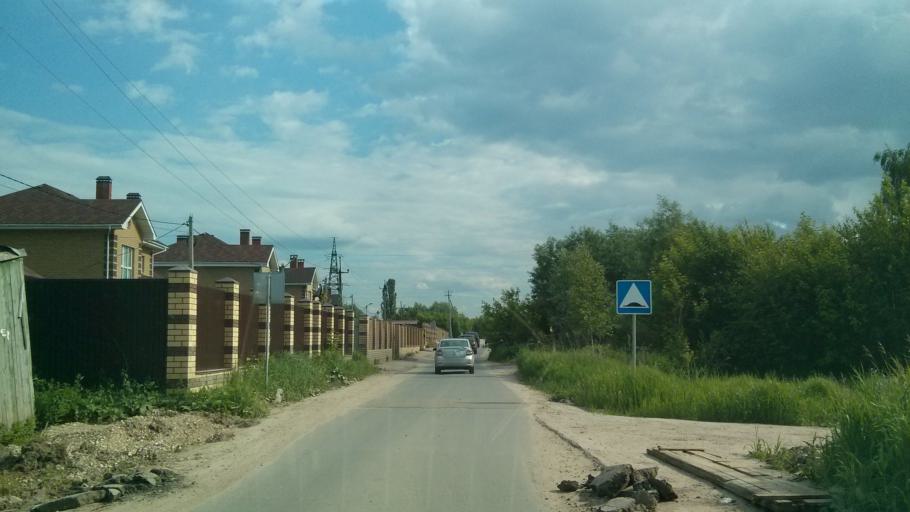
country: RU
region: Nizjnij Novgorod
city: Afonino
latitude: 56.2827
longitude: 44.1016
